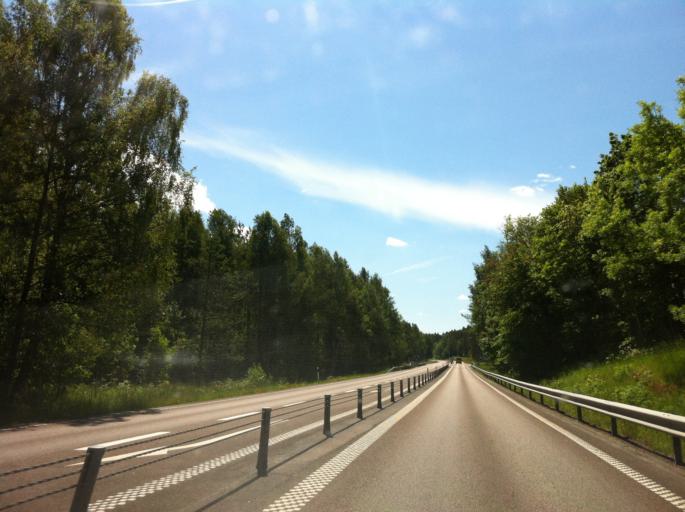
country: SE
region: Vaestra Goetaland
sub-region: Melleruds Kommun
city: Mellerud
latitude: 58.8180
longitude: 12.5233
